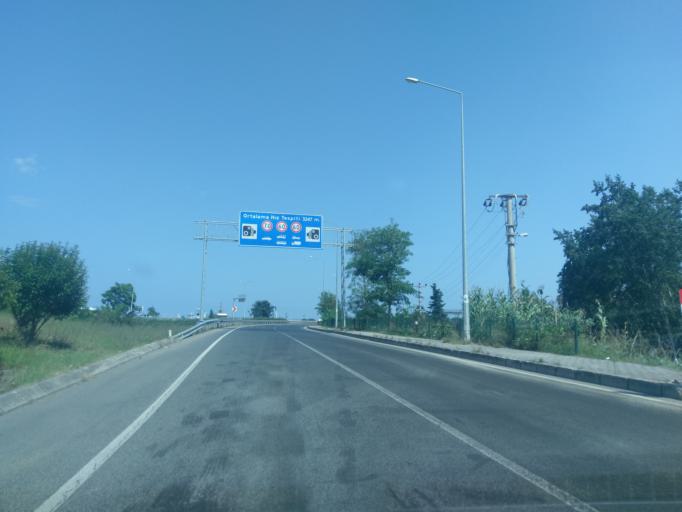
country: TR
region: Ordu
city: Ordu
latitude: 41.0164
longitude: 37.8467
